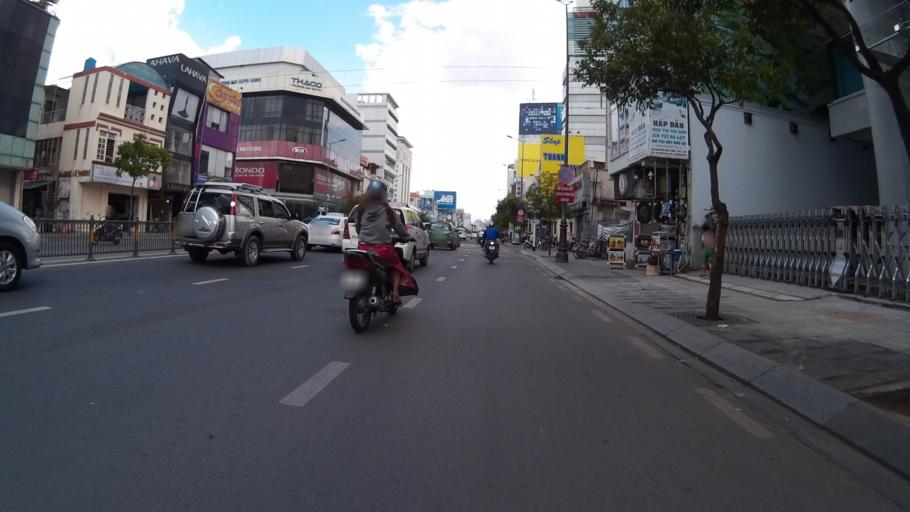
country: VN
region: Ho Chi Minh City
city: Quan Phu Nhuan
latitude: 10.7963
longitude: 106.6740
